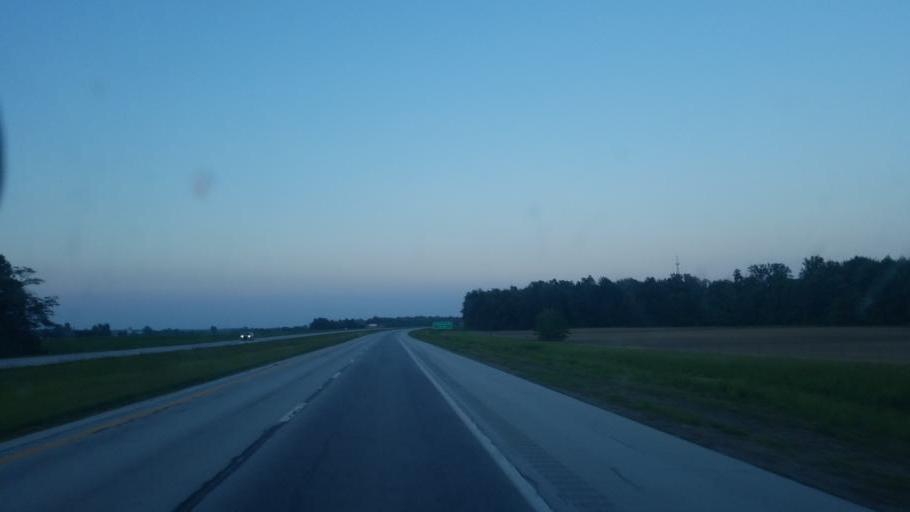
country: US
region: Ohio
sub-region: Hardin County
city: Forest
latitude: 40.8267
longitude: -83.4888
